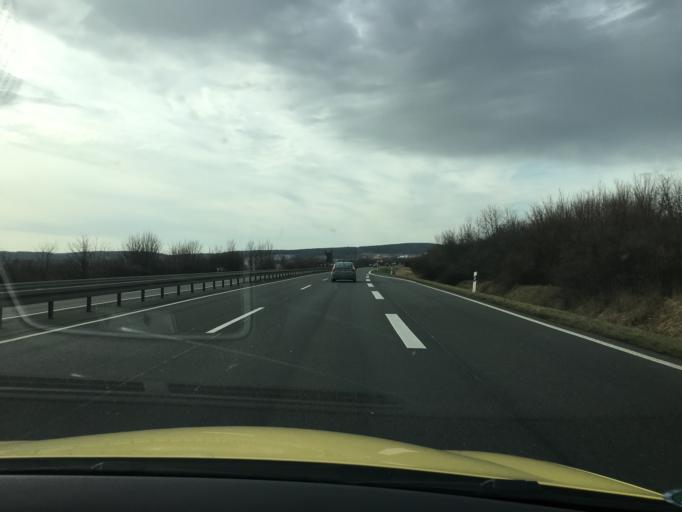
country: DE
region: Thuringia
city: Monchenholzhausen
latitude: 50.9759
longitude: 11.0922
